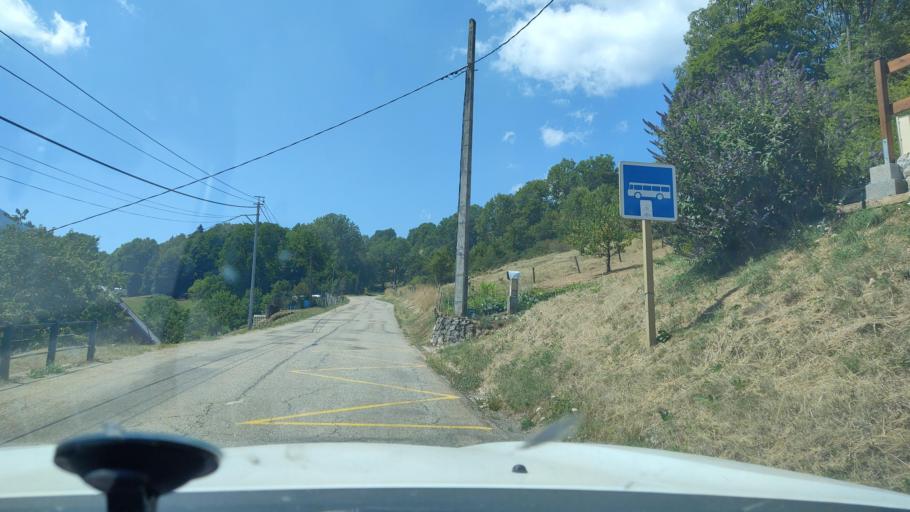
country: FR
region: Rhone-Alpes
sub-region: Departement de la Haute-Savoie
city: Cusy
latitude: 45.6738
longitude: 6.0445
